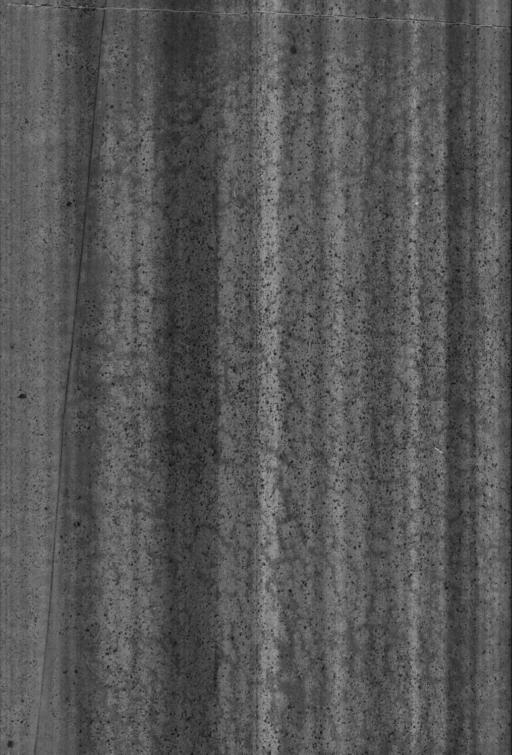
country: US
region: Maryland
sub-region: Prince George's County
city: Colmar Manor
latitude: 38.9180
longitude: -76.9515
